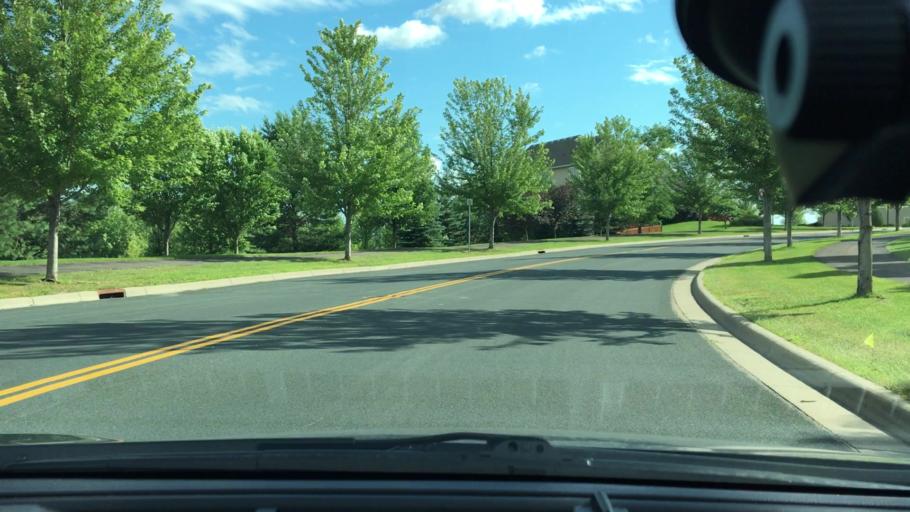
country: US
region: Minnesota
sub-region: Carver County
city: Victoria
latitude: 44.8594
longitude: -93.6796
